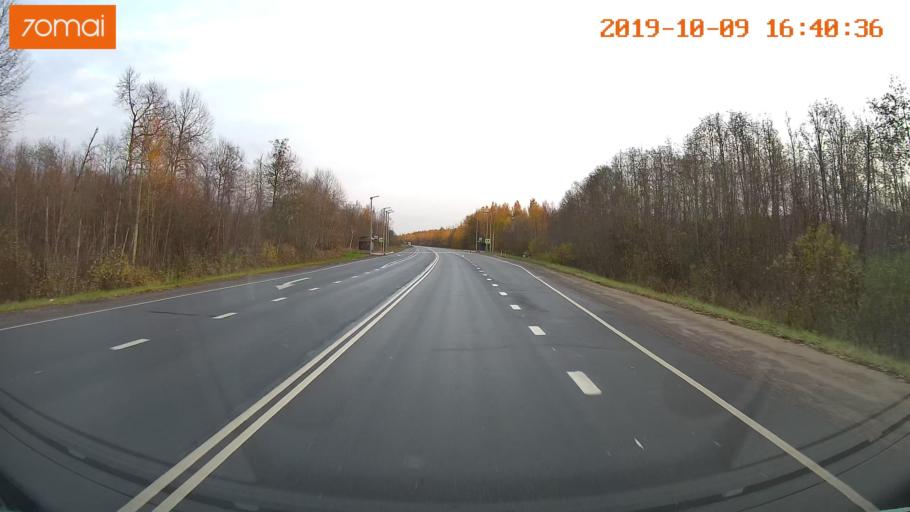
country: RU
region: Kostroma
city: Volgorechensk
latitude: 57.4816
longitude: 41.0634
